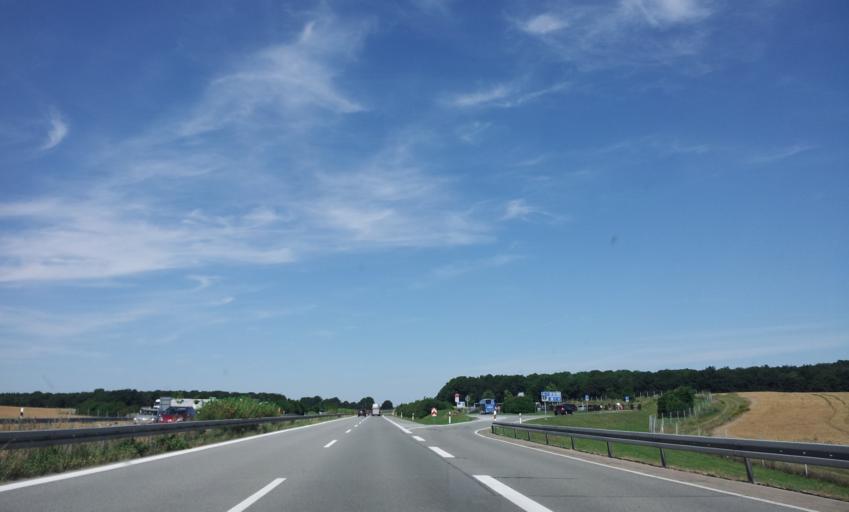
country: DE
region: Mecklenburg-Vorpommern
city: Neuenkirchen
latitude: 53.6179
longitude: 13.3687
